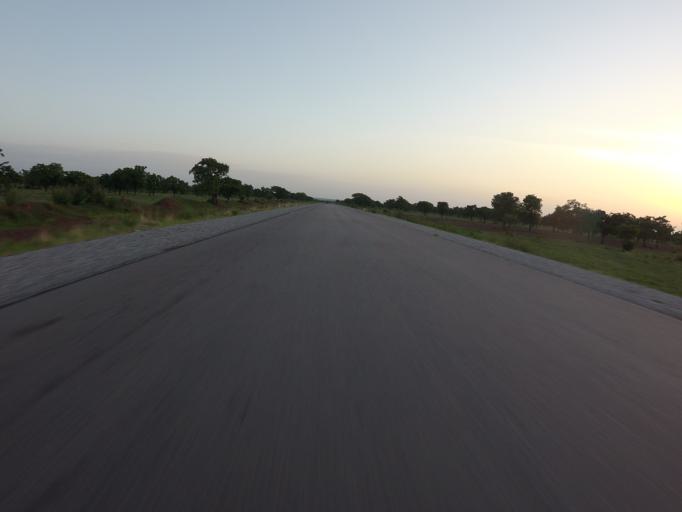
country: GH
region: Northern
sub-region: Yendi
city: Yendi
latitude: 9.9454
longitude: -0.1616
